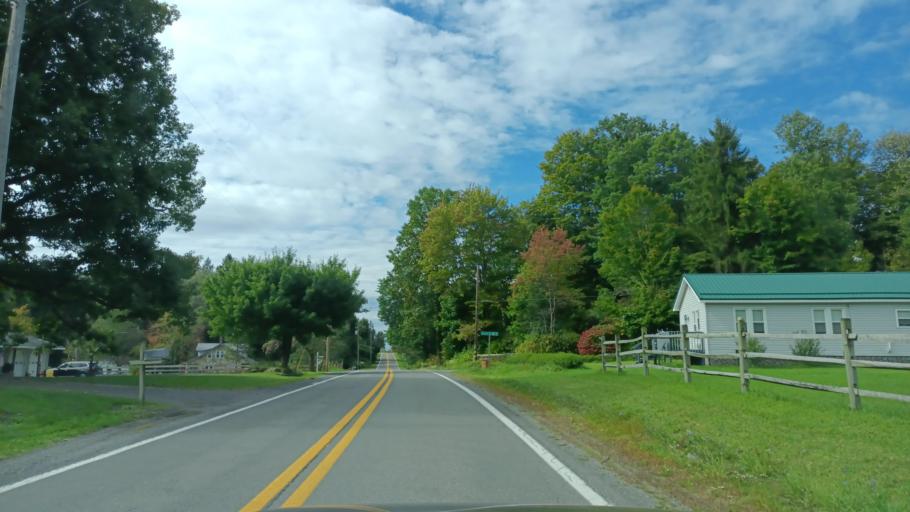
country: US
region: West Virginia
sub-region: Preston County
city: Terra Alta
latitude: 39.3134
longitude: -79.5865
